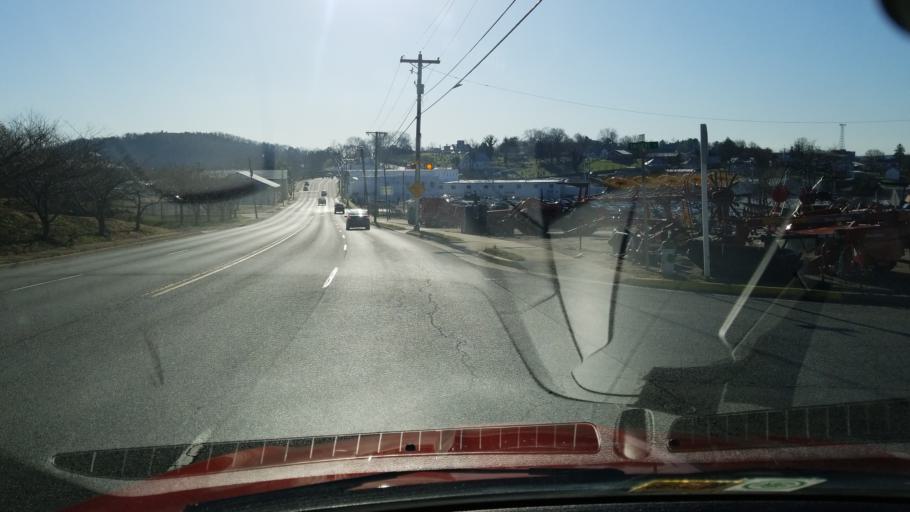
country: US
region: Virginia
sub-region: Franklin County
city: Rocky Mount
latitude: 37.0032
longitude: -79.8944
